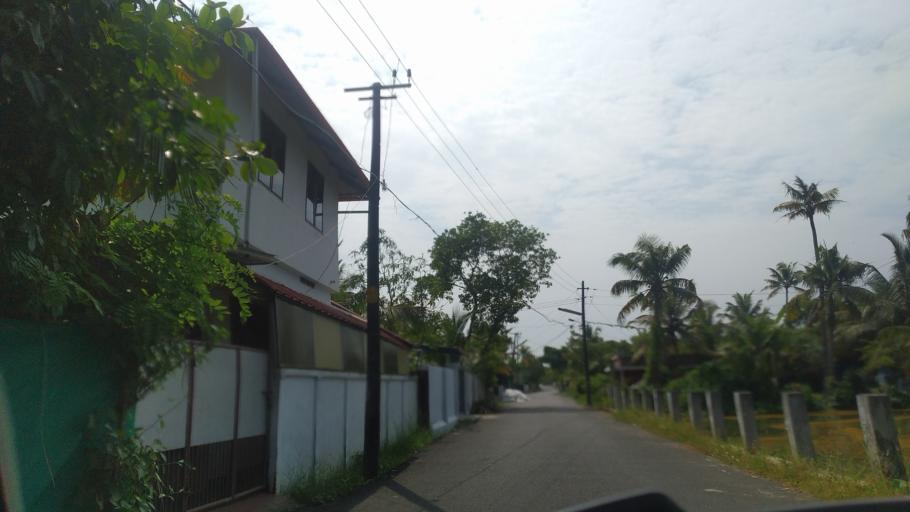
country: IN
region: Kerala
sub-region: Ernakulam
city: Elur
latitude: 10.0448
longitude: 76.2120
